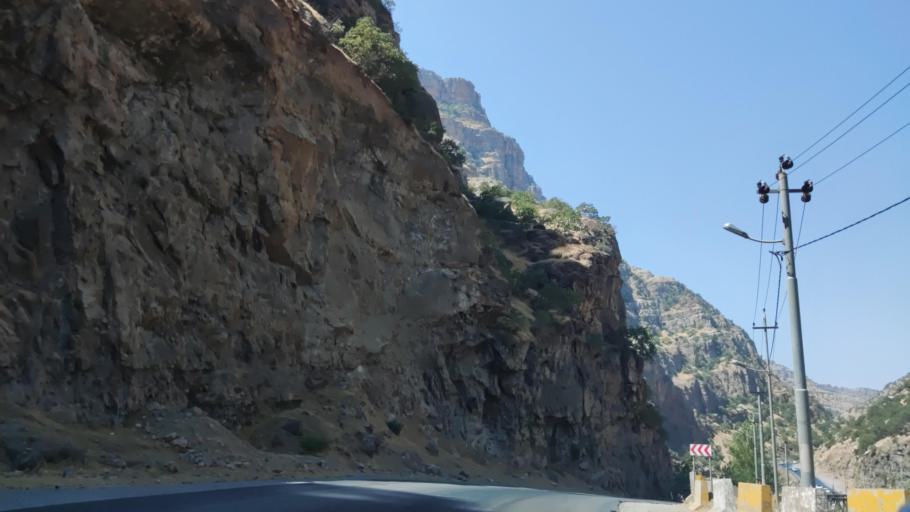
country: IQ
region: Arbil
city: Ruwandiz
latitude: 36.6317
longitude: 44.4893
